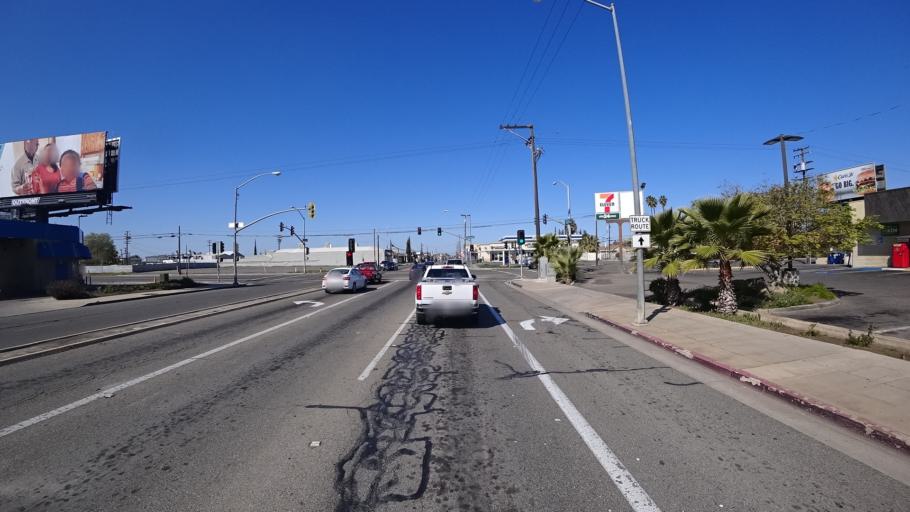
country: US
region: California
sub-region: Fresno County
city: Fresno
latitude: 36.7650
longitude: -119.7811
